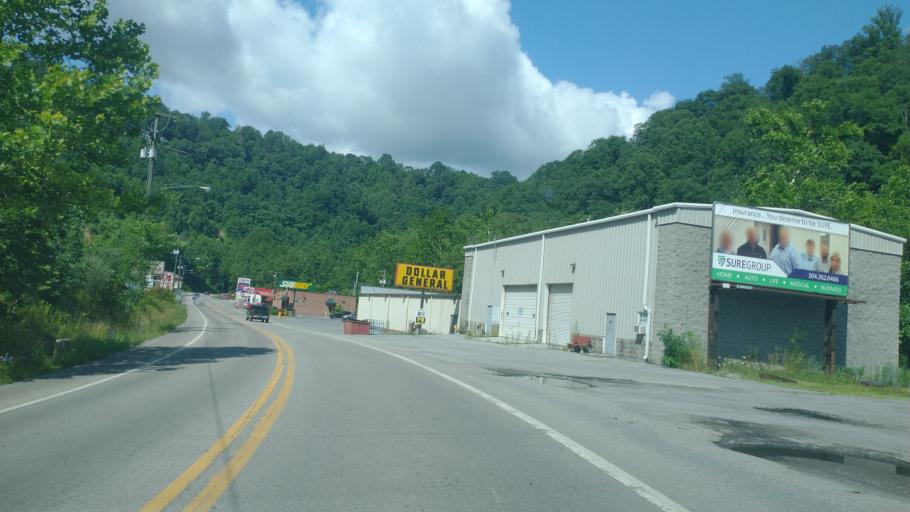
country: US
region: West Virginia
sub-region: McDowell County
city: Welch
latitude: 37.4307
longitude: -81.5536
